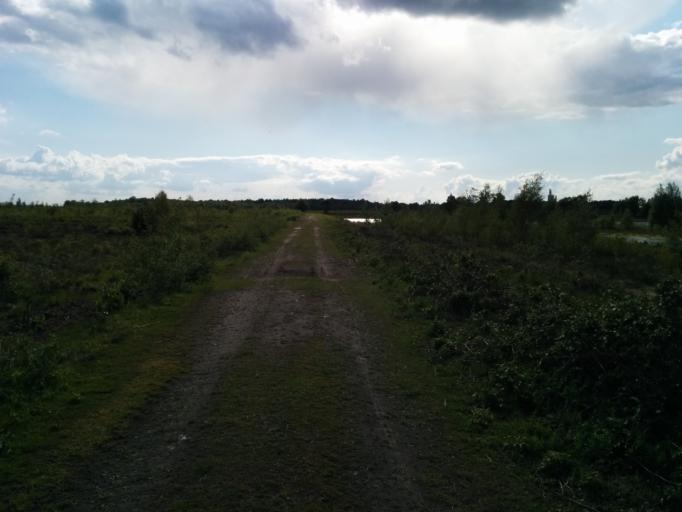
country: DE
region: Lower Saxony
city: Goldenstedt
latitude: 52.7271
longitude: 8.4113
